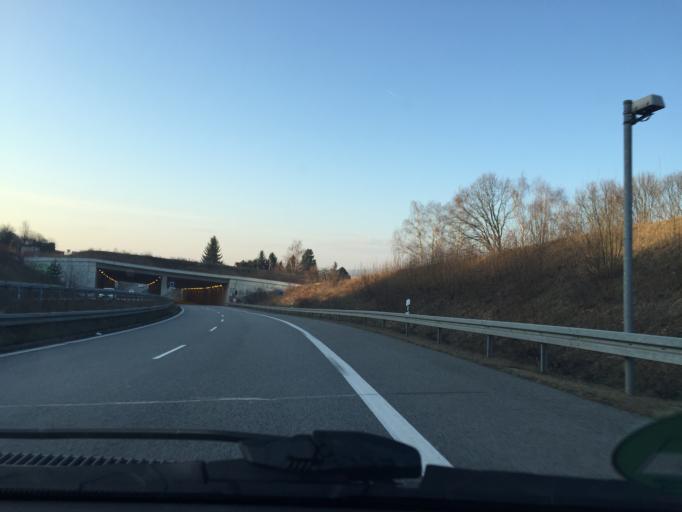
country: DE
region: Saxony
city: Pirna
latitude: 50.9520
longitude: 13.9231
